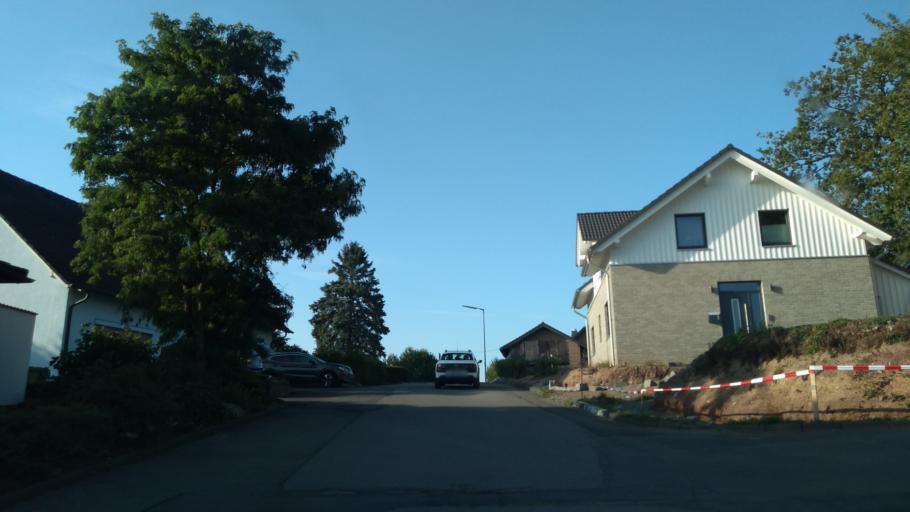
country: DE
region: North Rhine-Westphalia
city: Wiehl
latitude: 50.9695
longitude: 7.5074
